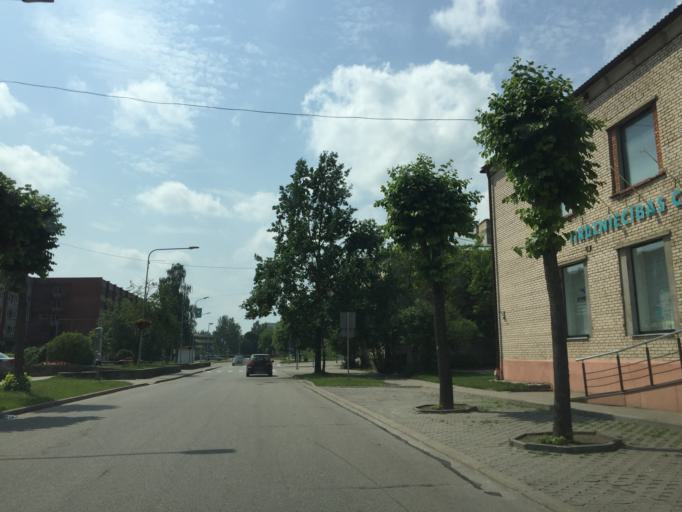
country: LV
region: Olaine
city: Olaine
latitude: 56.7850
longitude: 23.9380
